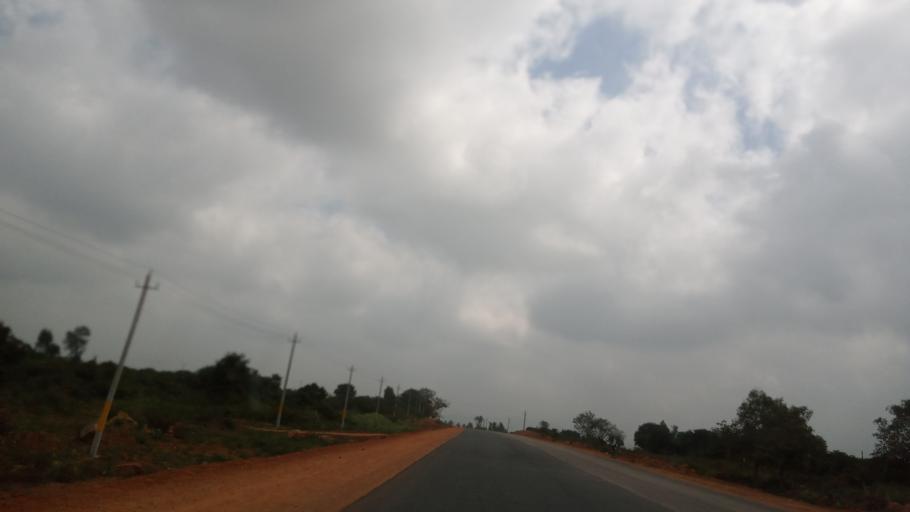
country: IN
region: Karnataka
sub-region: Kolar
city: Srinivaspur
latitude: 13.4459
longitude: 78.2409
